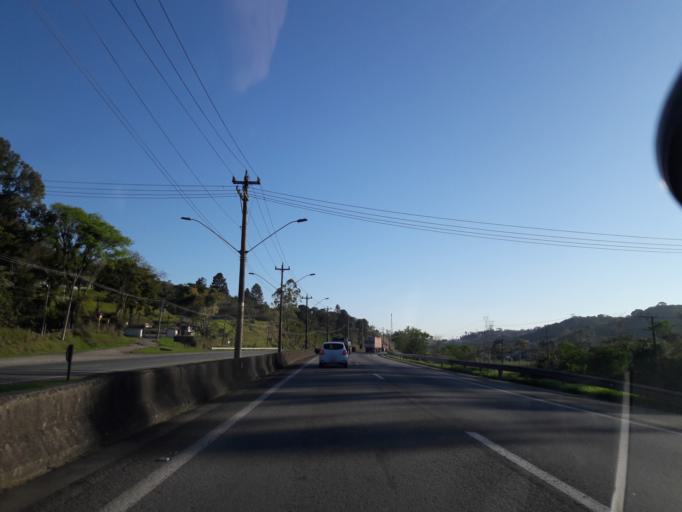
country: BR
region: Sao Paulo
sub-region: Sao Lourenco Da Serra
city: Sao Lourenco da Serra
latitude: -23.8778
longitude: -46.9683
